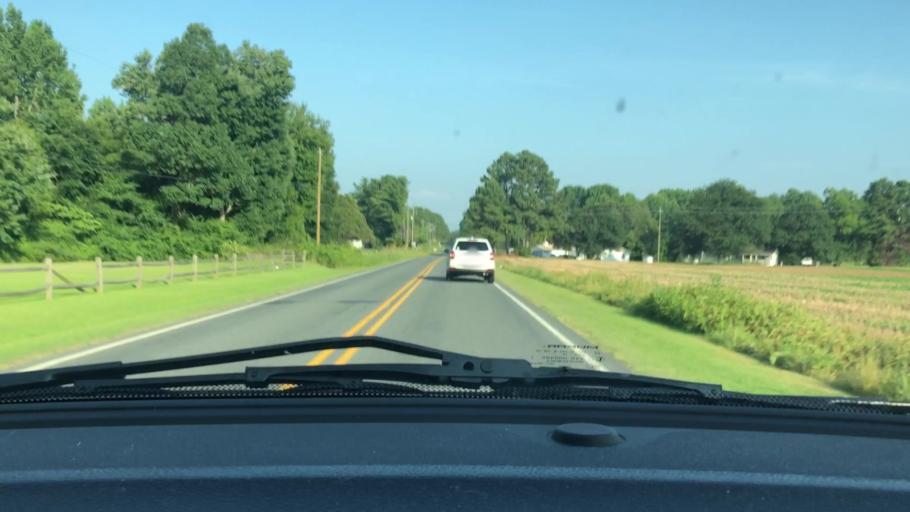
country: US
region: North Carolina
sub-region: Lee County
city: Broadway
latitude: 35.3636
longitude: -79.0910
